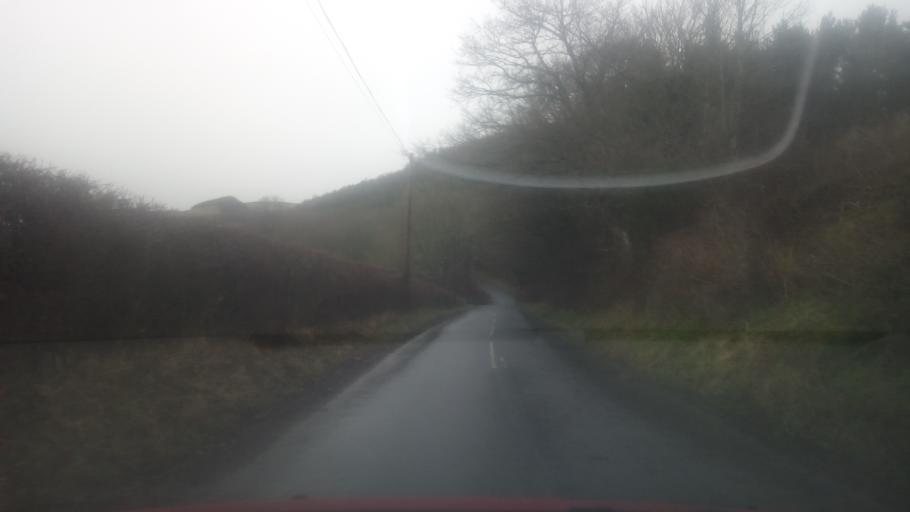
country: GB
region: Scotland
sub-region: The Scottish Borders
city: Earlston
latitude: 55.6176
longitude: -2.6648
